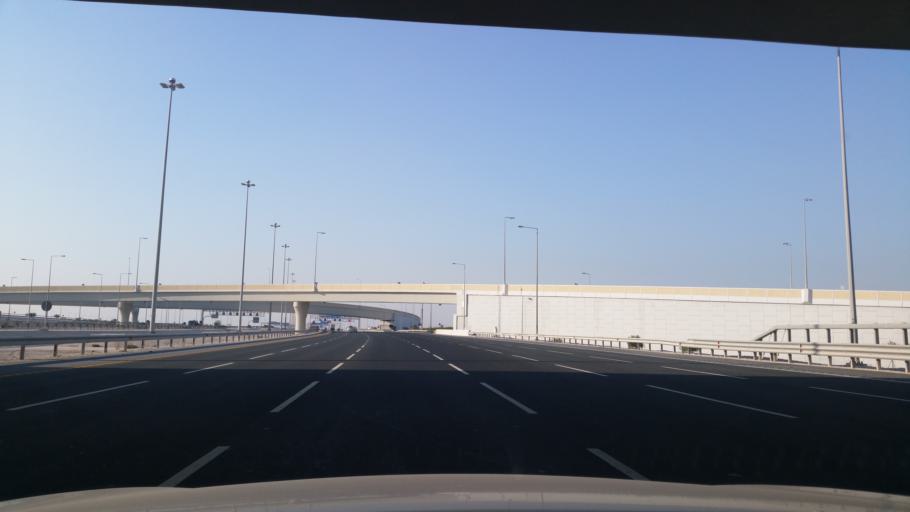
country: QA
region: Al Wakrah
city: Al Wakrah
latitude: 25.1322
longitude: 51.5862
